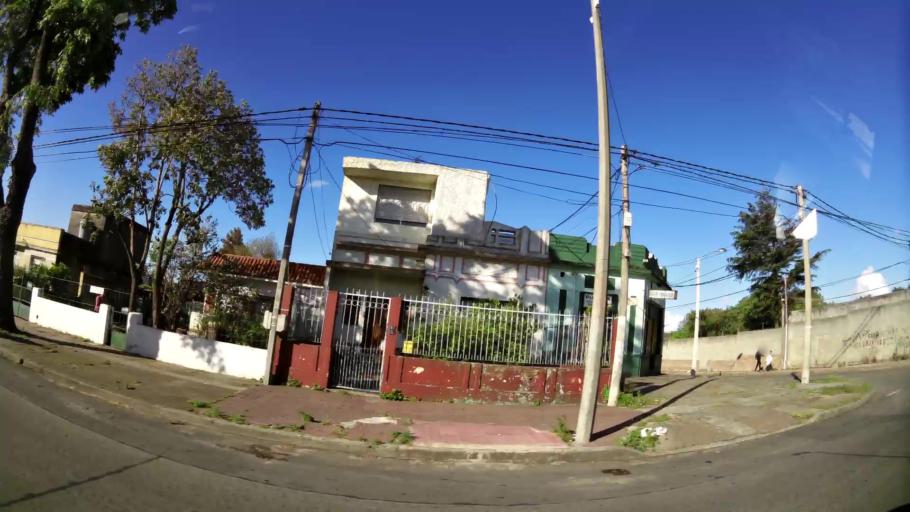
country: UY
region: Montevideo
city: Montevideo
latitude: -34.8543
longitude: -56.2353
